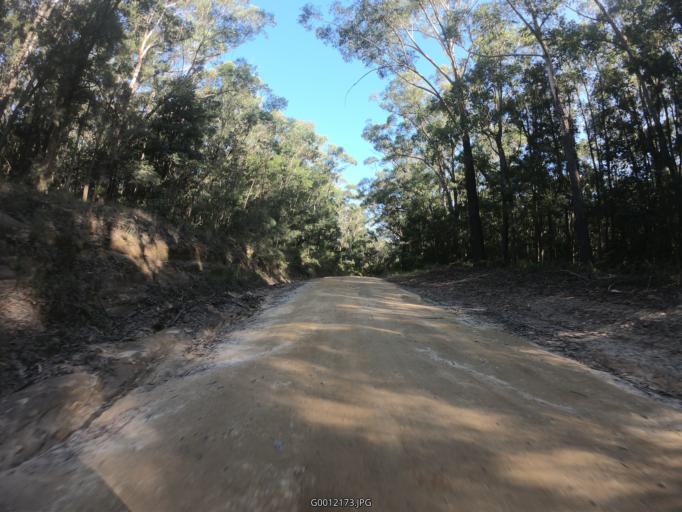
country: AU
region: New South Wales
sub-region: Lake Macquarie Shire
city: Cooranbong
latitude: -33.0820
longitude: 151.3572
